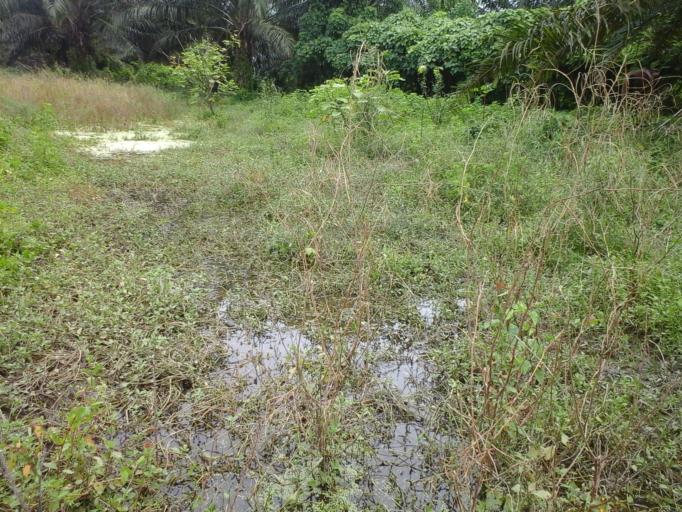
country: CO
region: Bolivar
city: San Pablo
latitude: 10.1604
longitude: -75.2751
